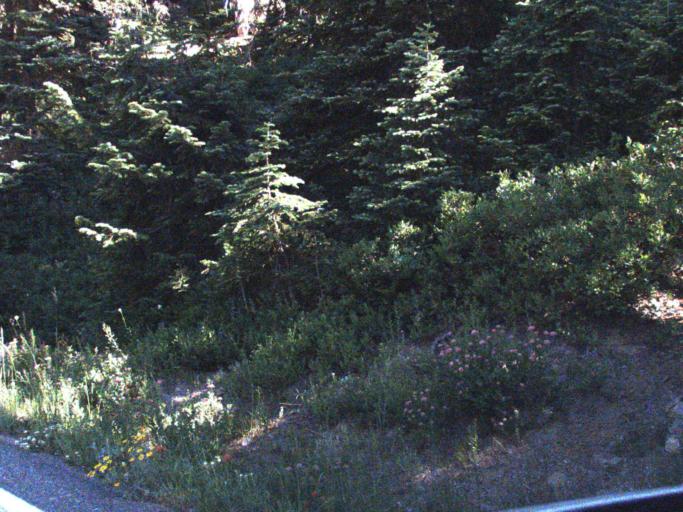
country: US
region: Washington
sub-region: King County
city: Enumclaw
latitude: 46.8674
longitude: -121.5236
